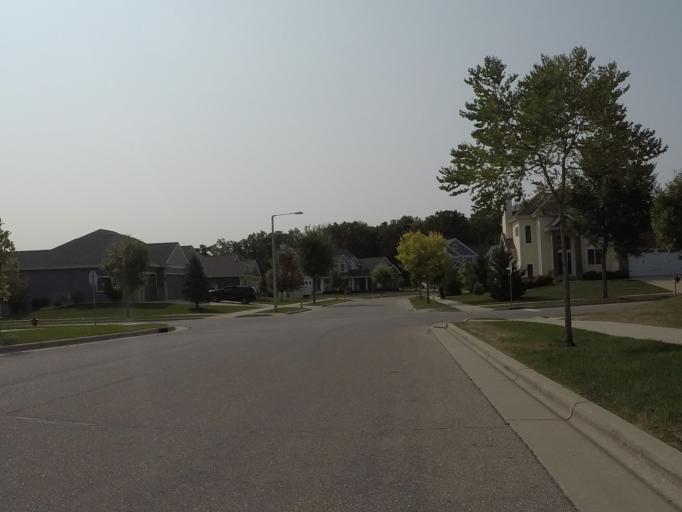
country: US
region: Wisconsin
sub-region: Dane County
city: Verona
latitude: 43.0302
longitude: -89.5450
